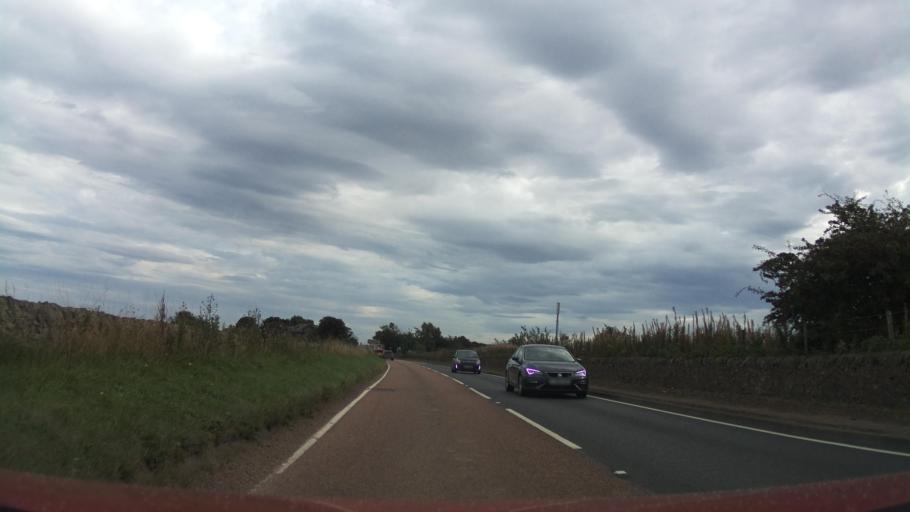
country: GB
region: Scotland
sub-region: Fife
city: Leuchars
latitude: 56.3868
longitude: -2.8960
